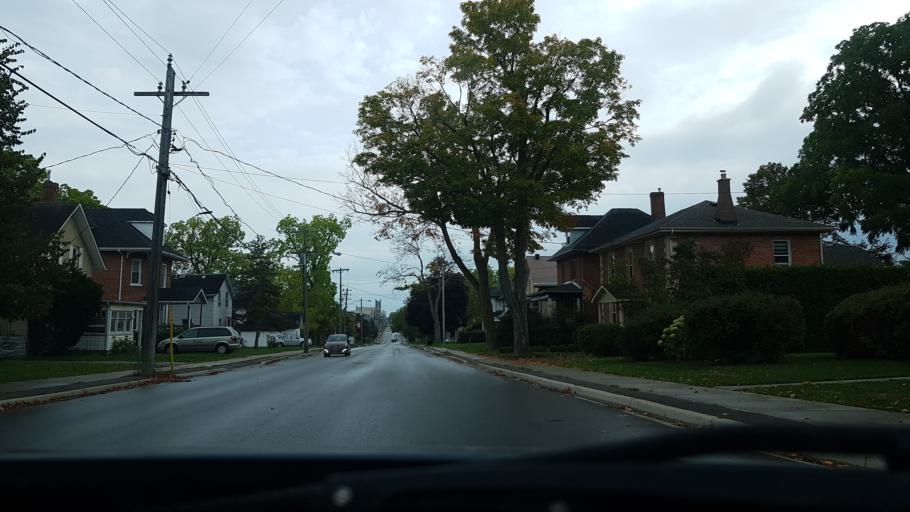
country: CA
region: Ontario
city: Omemee
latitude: 44.3620
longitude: -78.7403
